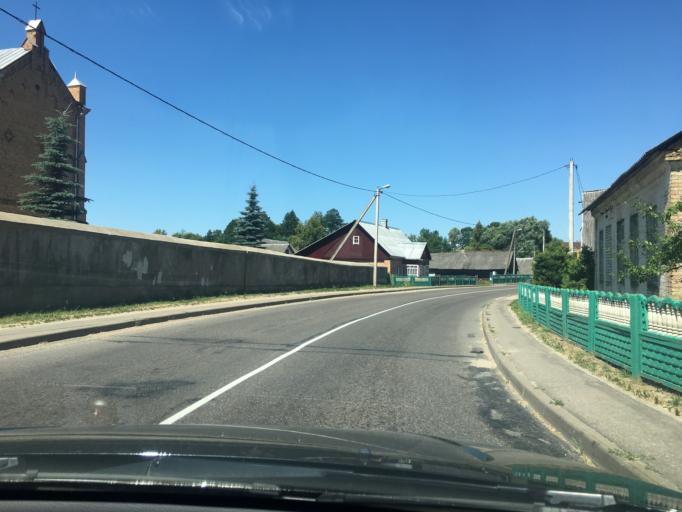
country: BY
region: Grodnenskaya
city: Hal'shany
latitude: 54.1555
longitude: 25.9075
